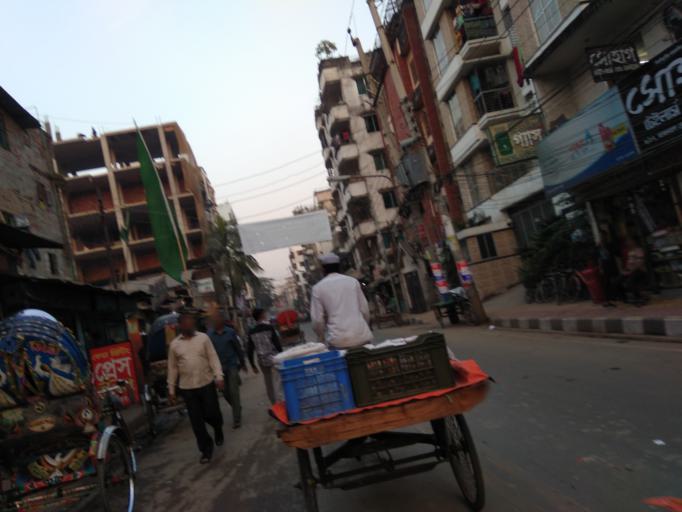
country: BD
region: Dhaka
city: Azimpur
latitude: 23.7665
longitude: 90.3622
